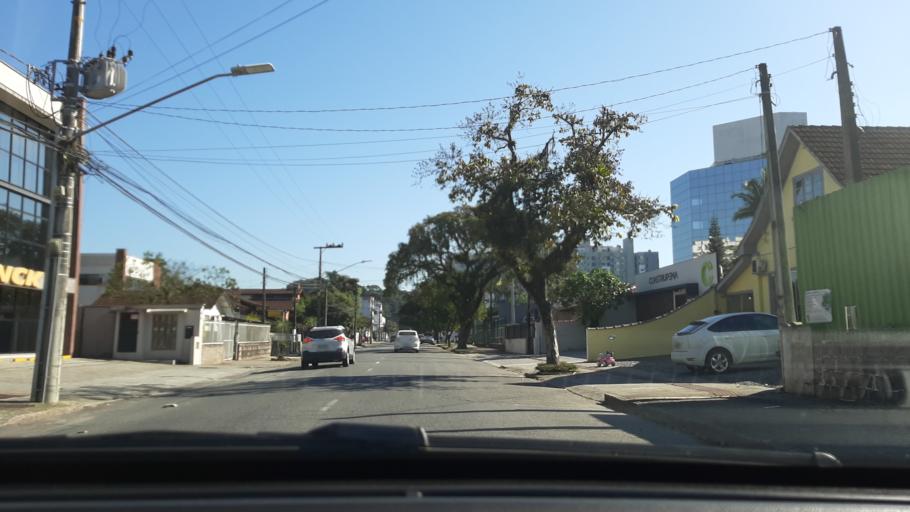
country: BR
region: Santa Catarina
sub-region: Joinville
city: Joinville
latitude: -26.3137
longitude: -48.8515
